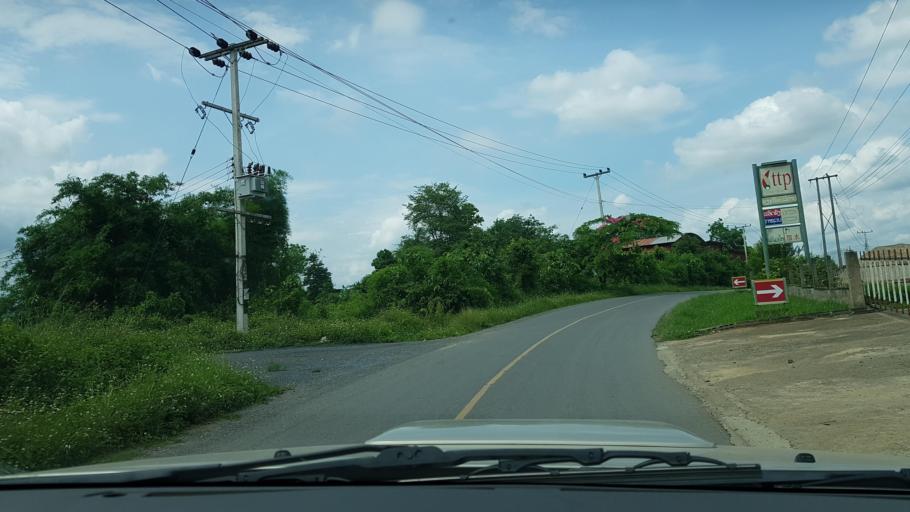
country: LA
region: Loungnamtha
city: Muang Nale
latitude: 20.1187
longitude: 101.4219
